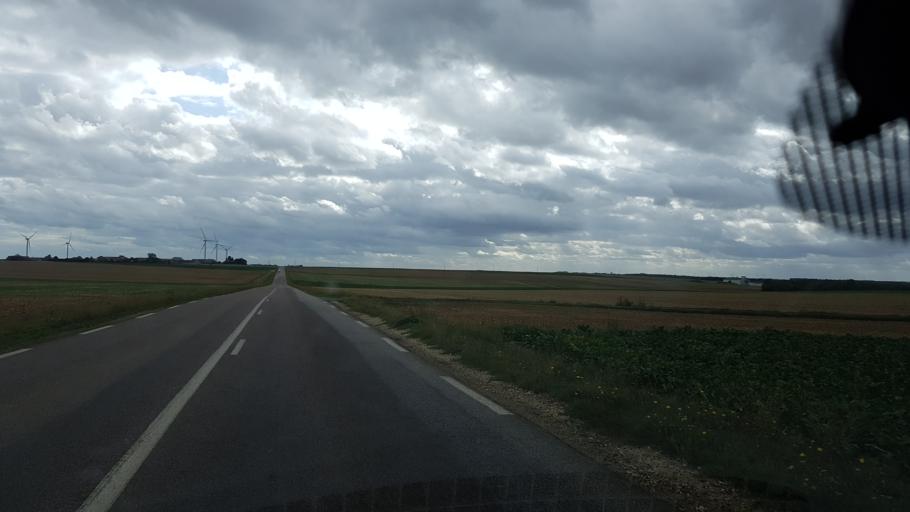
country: FR
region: Ile-de-France
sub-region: Departement de l'Essonne
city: Etampes
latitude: 48.4021
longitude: 2.1750
